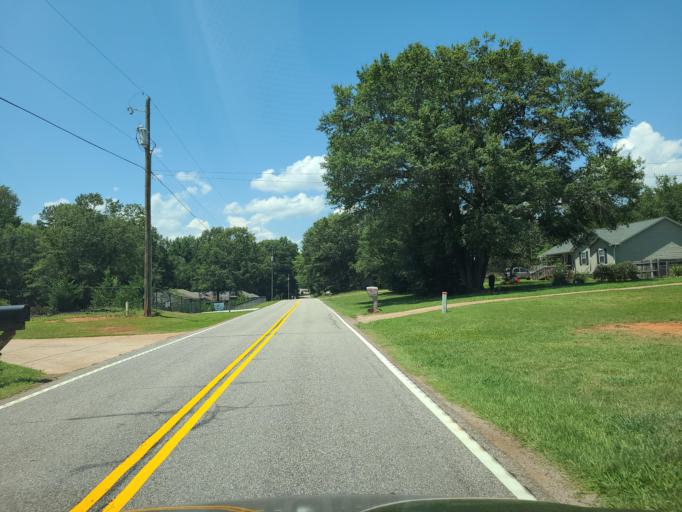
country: US
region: South Carolina
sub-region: Spartanburg County
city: Duncan
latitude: 34.9682
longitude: -82.1730
